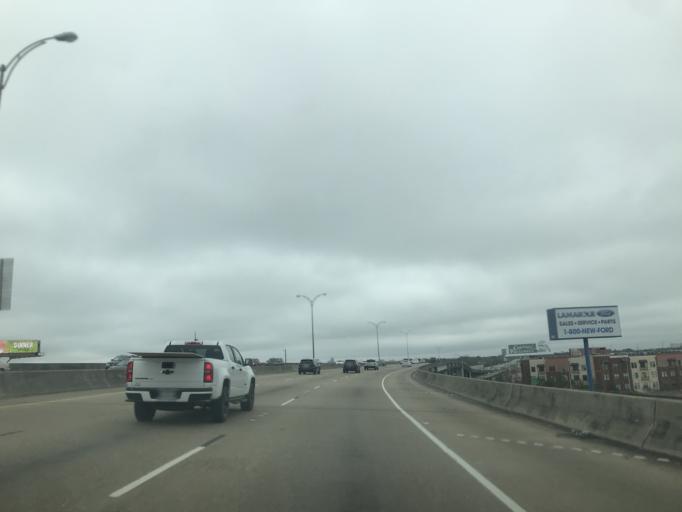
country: US
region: Louisiana
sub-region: Orleans Parish
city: New Orleans
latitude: 29.9686
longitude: -90.1079
